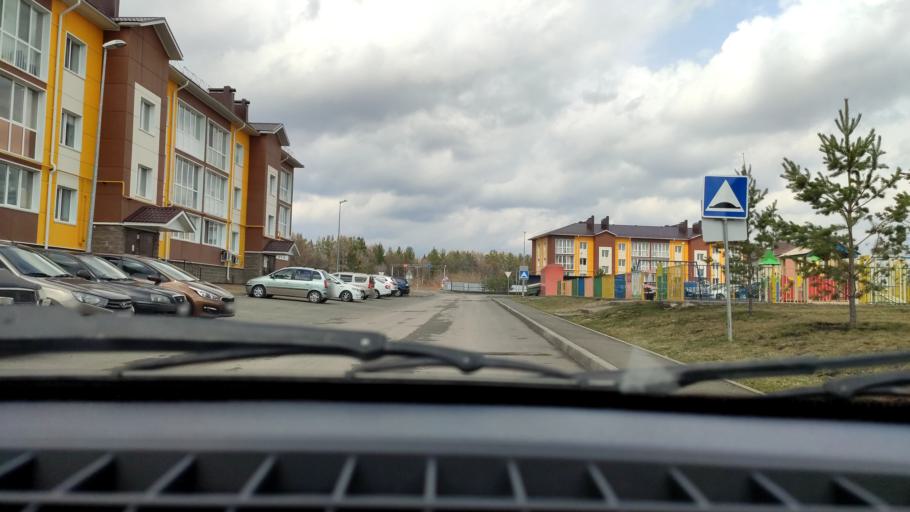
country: RU
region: Bashkortostan
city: Ufa
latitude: 54.5898
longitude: 55.9169
